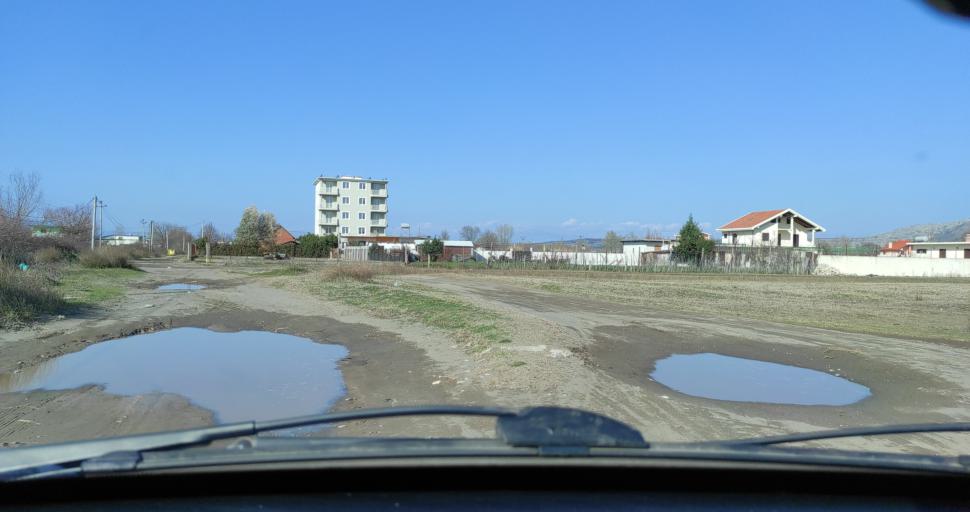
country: AL
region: Shkoder
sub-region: Rrethi i Shkodres
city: Velipoje
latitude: 41.8684
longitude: 19.4116
